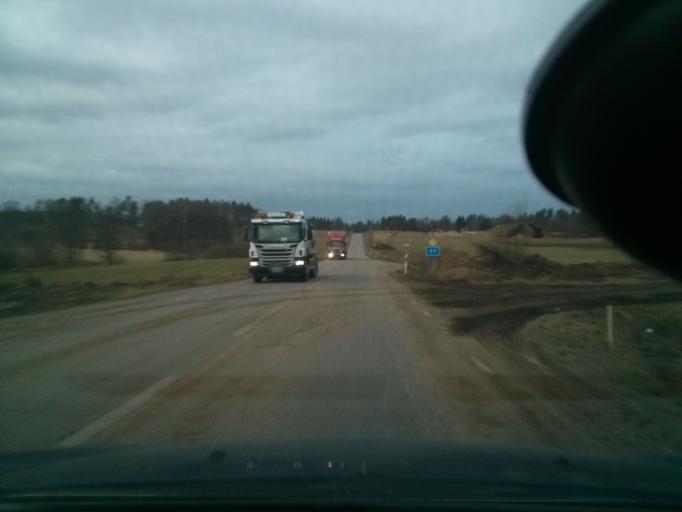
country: SE
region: Blekinge
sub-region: Ronneby Kommun
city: Brakne-Hoby
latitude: 56.3029
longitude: 15.1914
